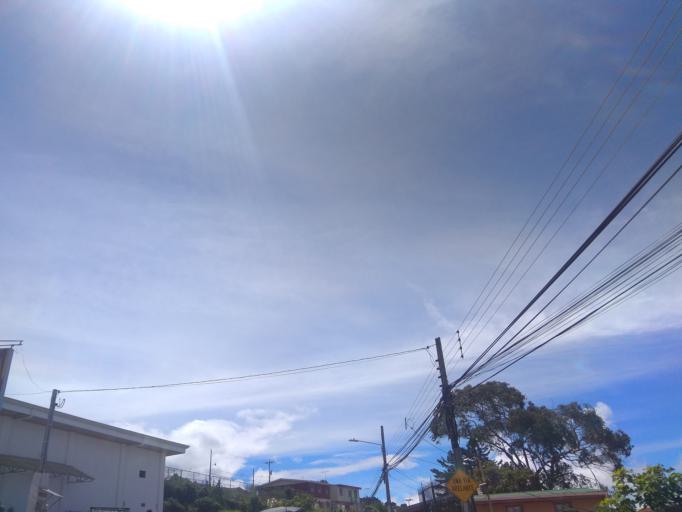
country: CR
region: Cartago
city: Cot
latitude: 9.9152
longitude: -83.8924
